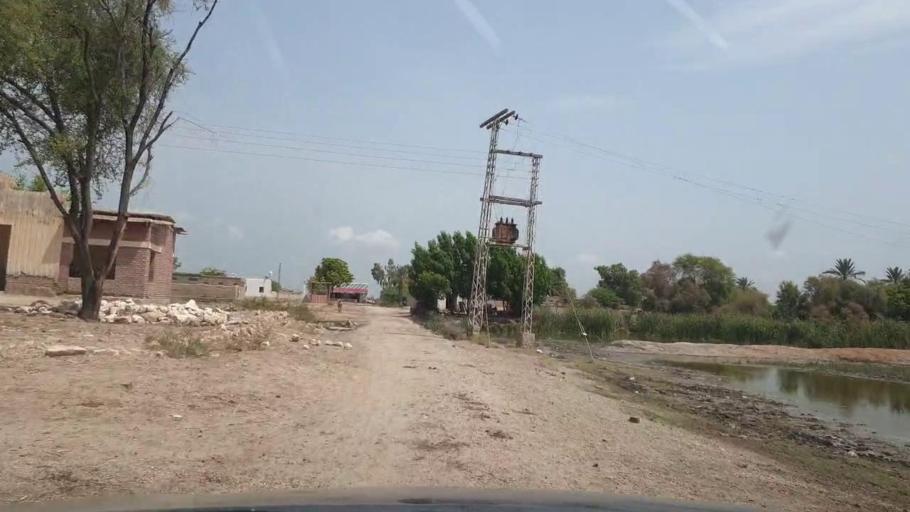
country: PK
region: Sindh
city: Ratodero
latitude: 27.8965
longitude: 68.3148
